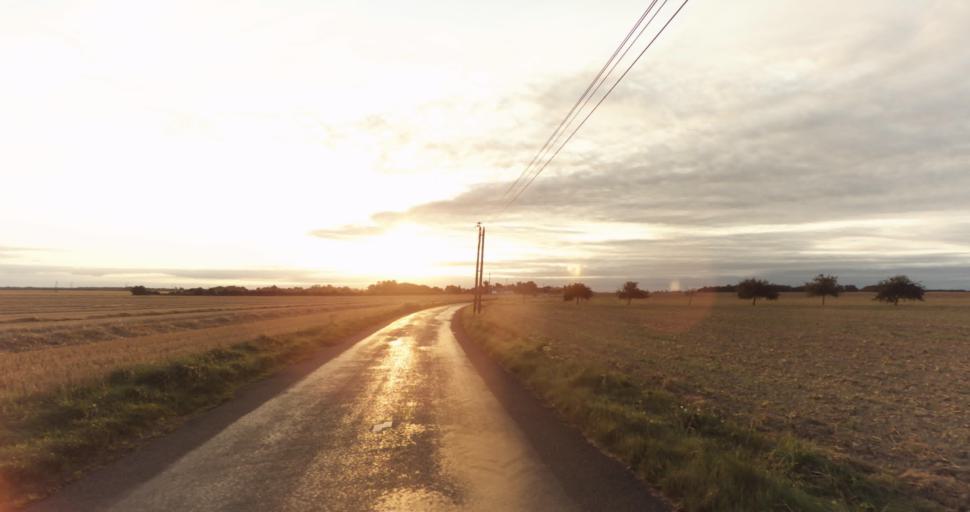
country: FR
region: Haute-Normandie
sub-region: Departement de l'Eure
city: La Madeleine-de-Nonancourt
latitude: 48.8734
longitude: 1.2145
